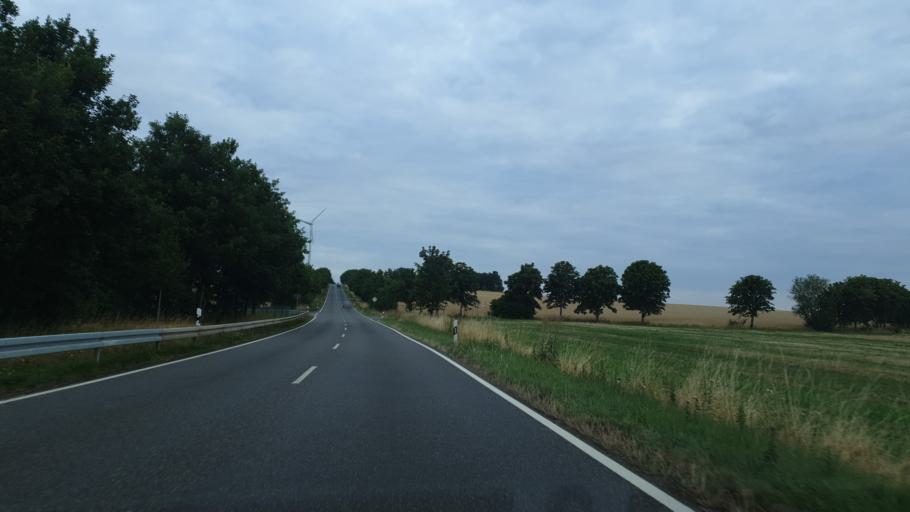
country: DE
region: Saxony
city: Sankt Egidien
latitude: 50.8082
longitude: 12.6323
